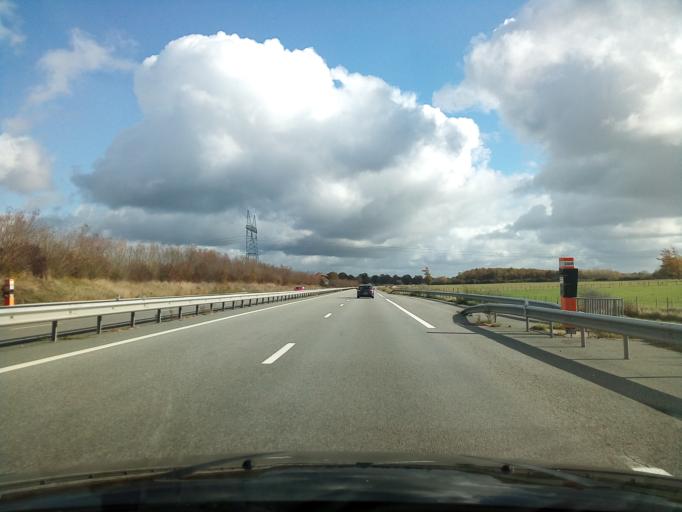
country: FR
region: Limousin
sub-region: Departement de la Creuse
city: Gouzon
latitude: 46.1978
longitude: 2.1987
